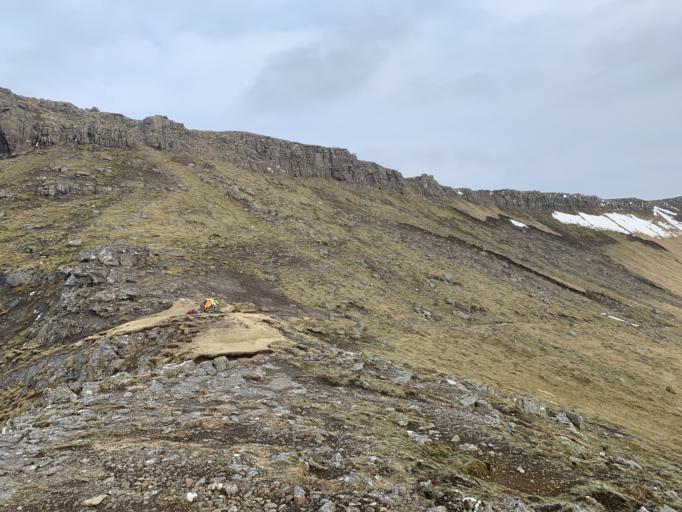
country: FO
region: Vagar
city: Sorvagur
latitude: 62.1027
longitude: -7.4225
